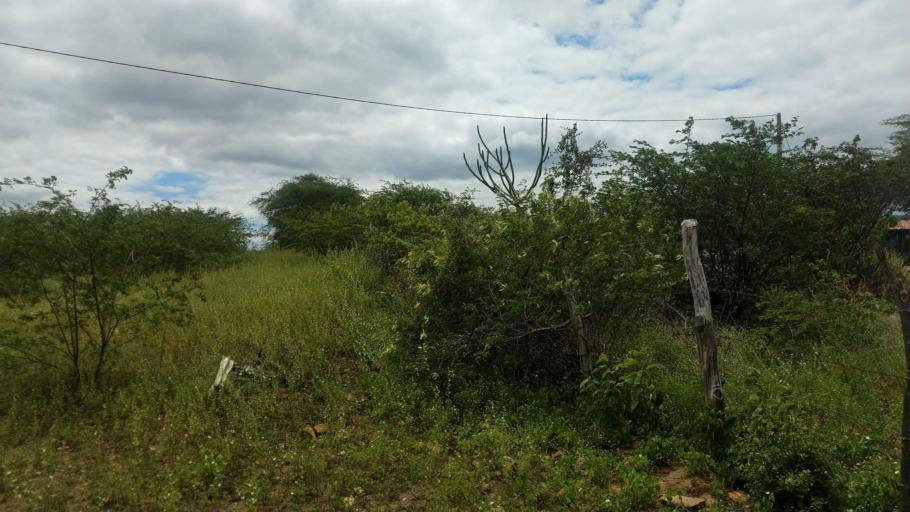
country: BR
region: Rio Grande do Norte
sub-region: Sao Tome
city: Sao Tome
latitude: -5.9643
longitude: -35.9215
